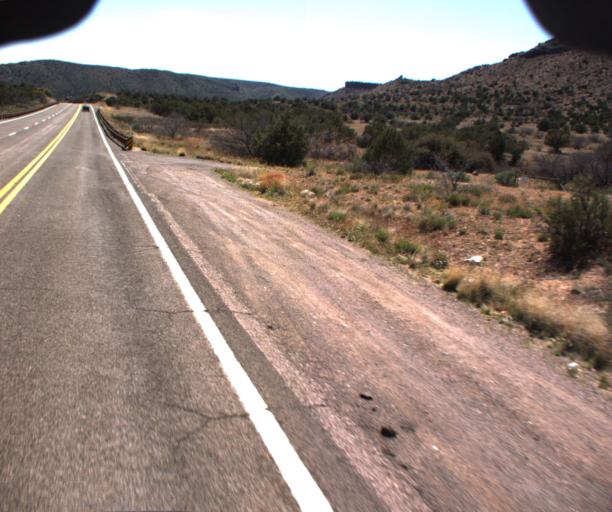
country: US
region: Arizona
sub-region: Mohave County
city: Peach Springs
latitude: 35.4372
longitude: -113.6468
